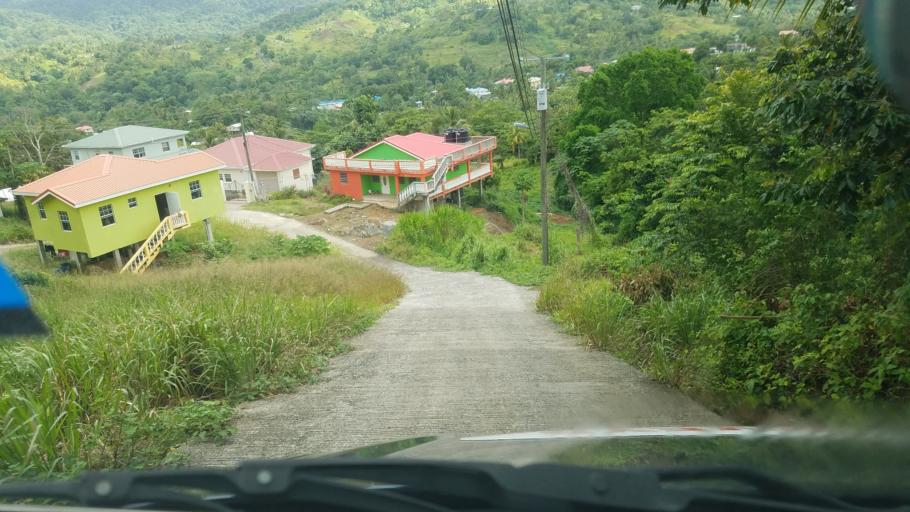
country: LC
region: Castries Quarter
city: Bisee
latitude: 14.0022
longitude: -60.9350
